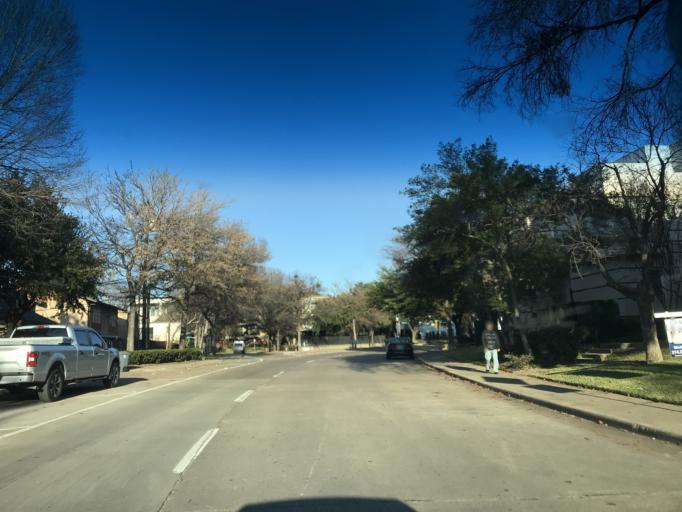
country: US
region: Texas
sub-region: Dallas County
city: Highland Park
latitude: 32.8174
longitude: -96.8080
